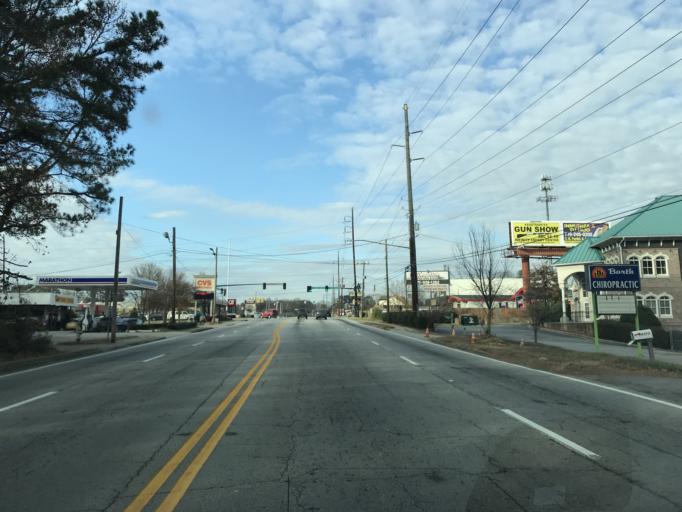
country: US
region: Georgia
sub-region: DeKalb County
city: Tucker
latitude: 33.8800
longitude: -84.2189
